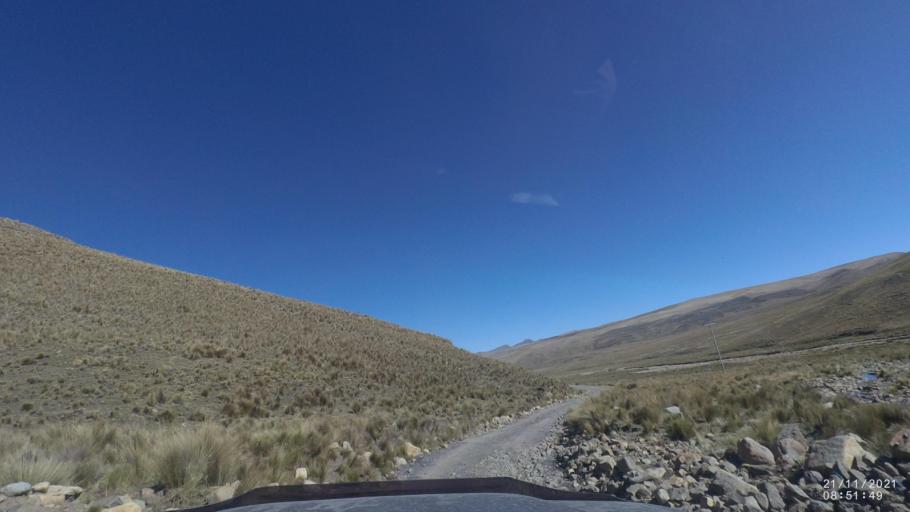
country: BO
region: Cochabamba
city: Cochabamba
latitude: -17.2165
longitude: -66.2378
